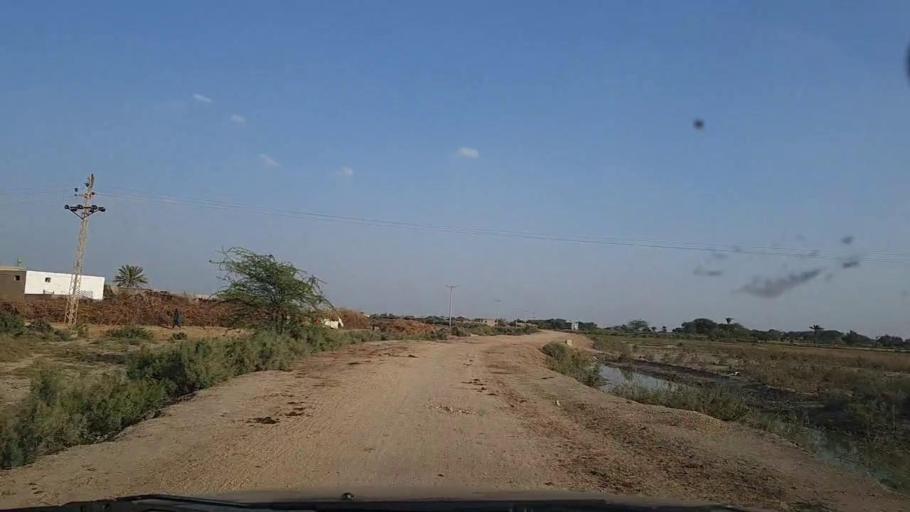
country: PK
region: Sindh
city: Daro Mehar
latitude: 24.7499
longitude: 68.0902
